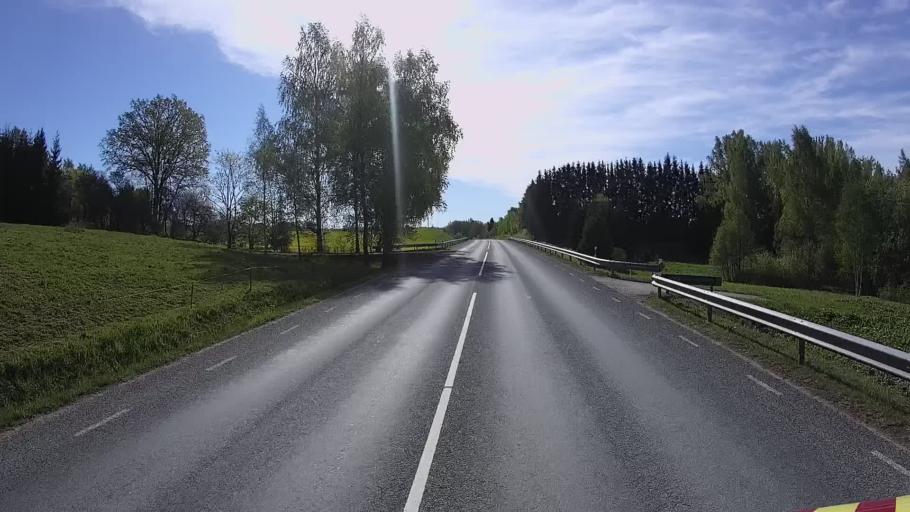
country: EE
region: Polvamaa
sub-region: Polva linn
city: Polva
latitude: 58.1605
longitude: 27.1616
